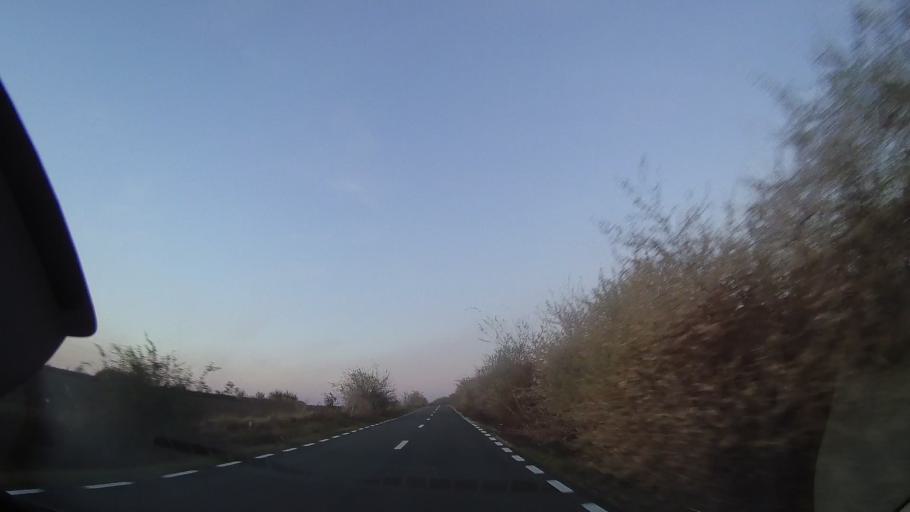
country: RO
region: Constanta
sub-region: Comuna Cobadin
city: Cobadin
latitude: 44.0331
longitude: 28.2605
